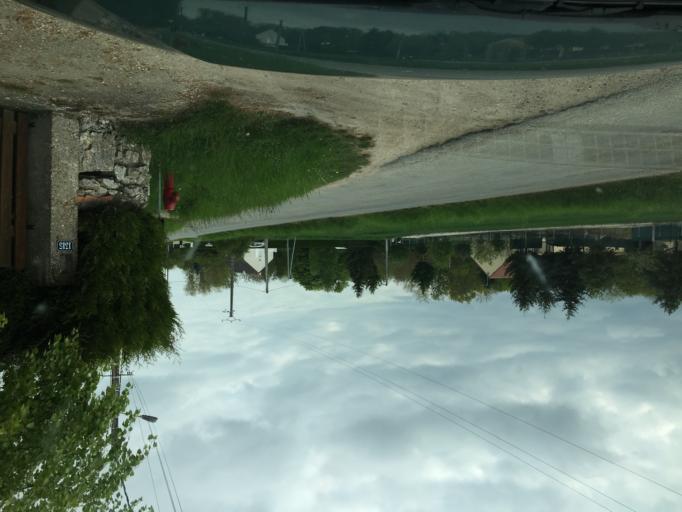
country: FR
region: Centre
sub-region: Departement du Loiret
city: Huisseau-sur-Mauves
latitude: 47.8642
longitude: 1.6956
